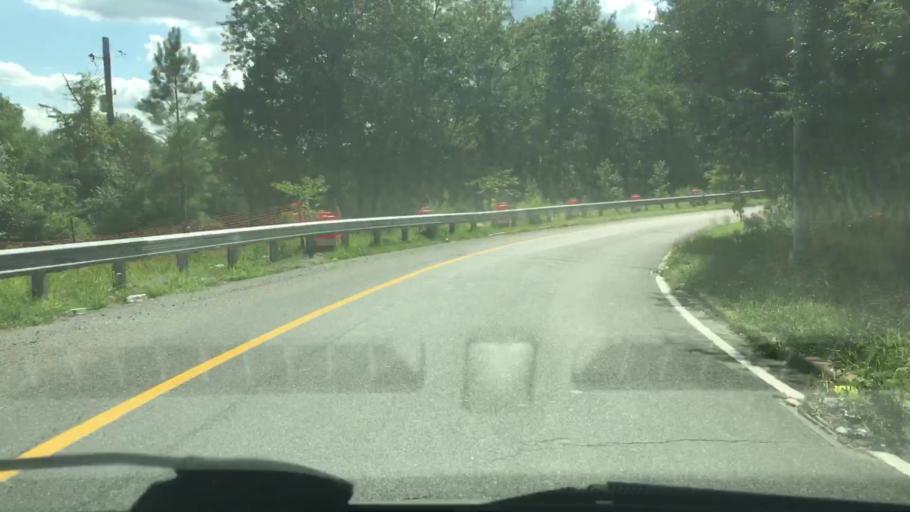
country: US
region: Maryland
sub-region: Prince George's County
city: Camp Springs
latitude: 38.8185
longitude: -76.9199
